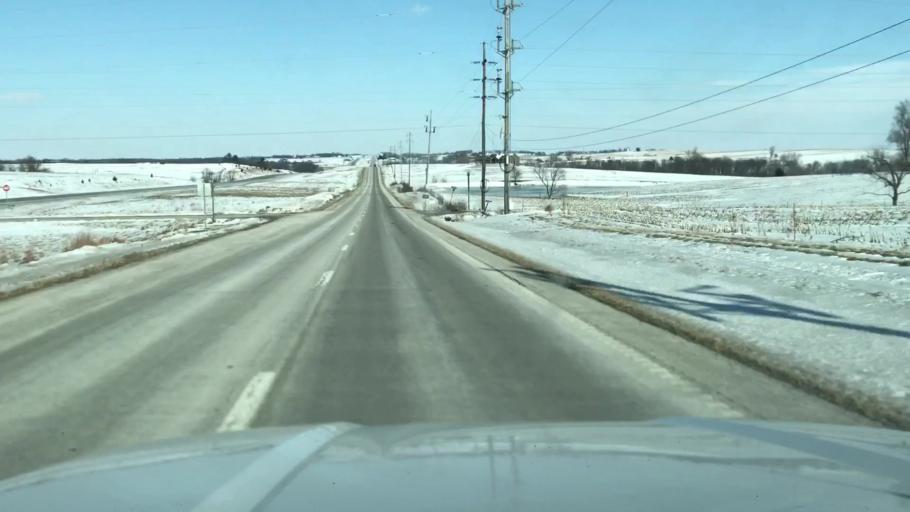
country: US
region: Missouri
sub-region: Andrew County
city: Savannah
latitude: 40.1275
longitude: -94.8695
